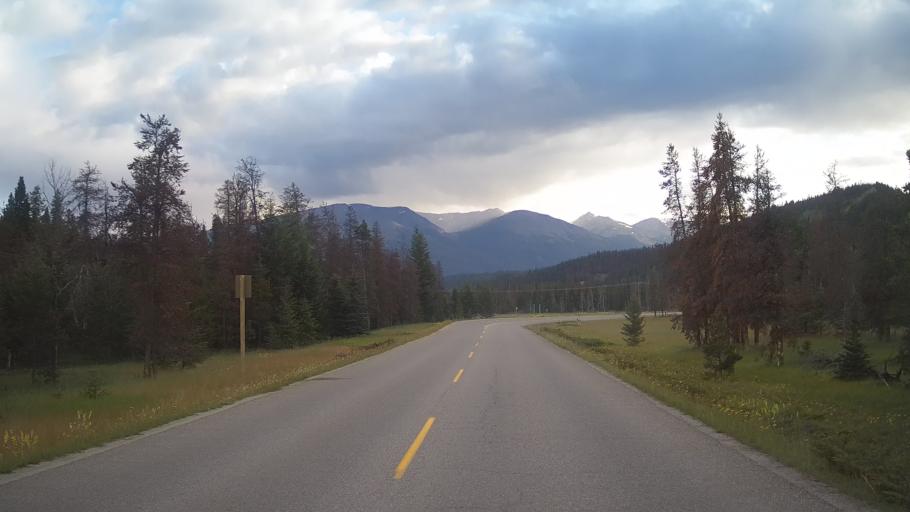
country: CA
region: Alberta
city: Jasper Park Lodge
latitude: 52.9109
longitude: -118.0537
